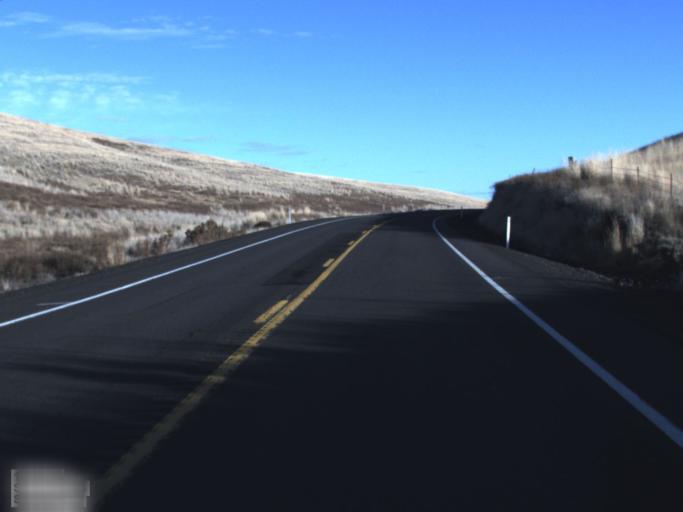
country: US
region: Washington
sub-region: Garfield County
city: Pomeroy
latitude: 46.6965
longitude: -117.7905
